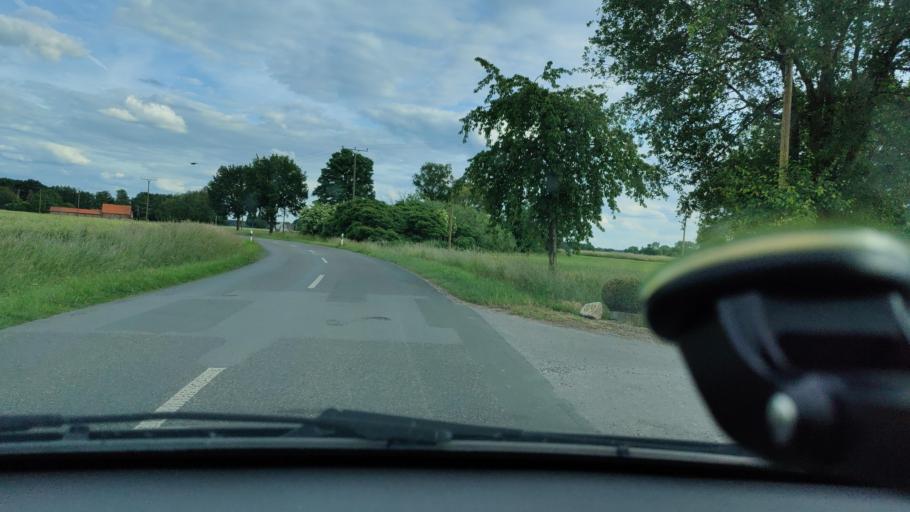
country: DE
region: North Rhine-Westphalia
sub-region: Regierungsbezirk Dusseldorf
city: Goch
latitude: 51.6373
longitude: 6.1499
